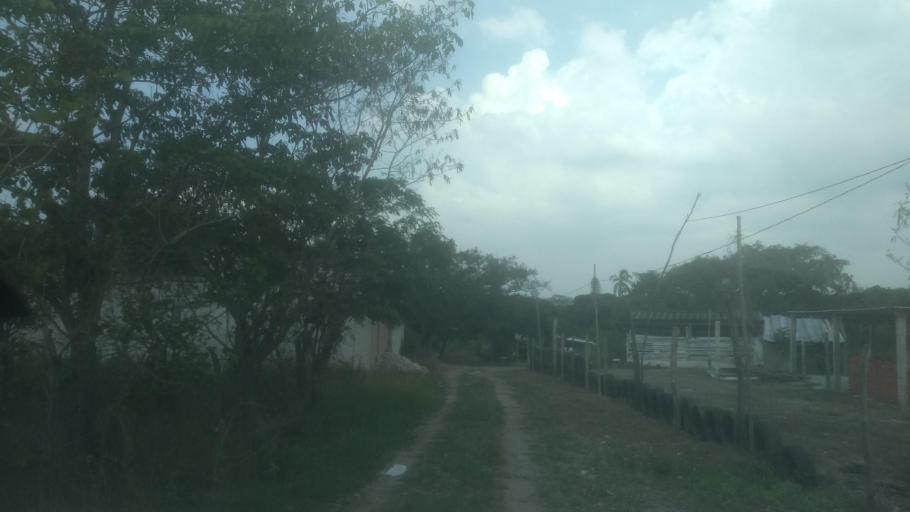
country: MX
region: Veracruz
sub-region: Emiliano Zapata
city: Plan del Rio
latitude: 19.4320
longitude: -96.6977
